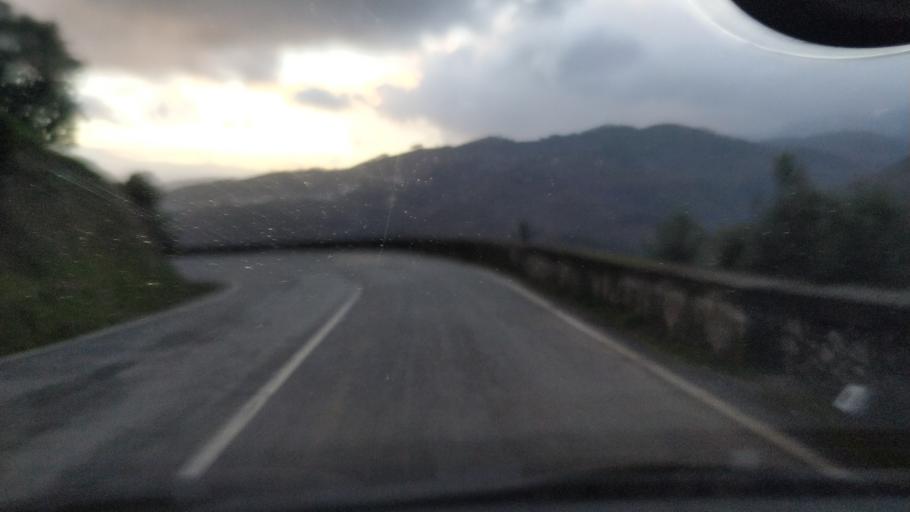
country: PT
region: Vila Real
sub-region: Santa Marta de Penaguiao
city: Santa Marta de Penaguiao
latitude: 41.2461
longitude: -7.7683
